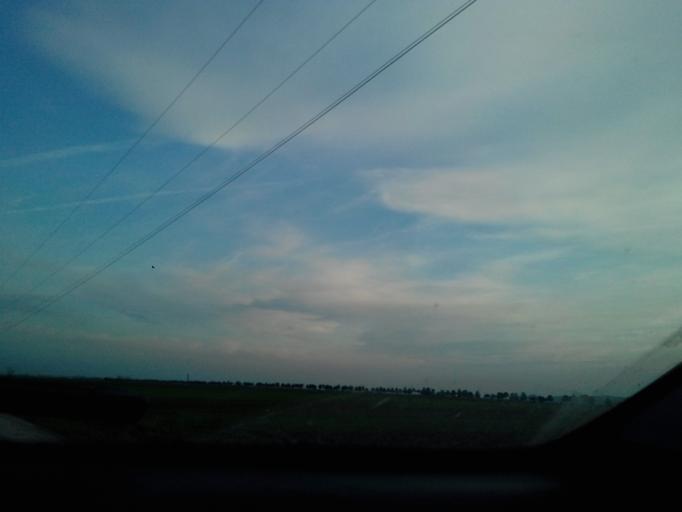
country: RO
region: Prahova
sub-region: Comuna Banesti
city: Urleta
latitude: 45.0751
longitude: 25.7820
